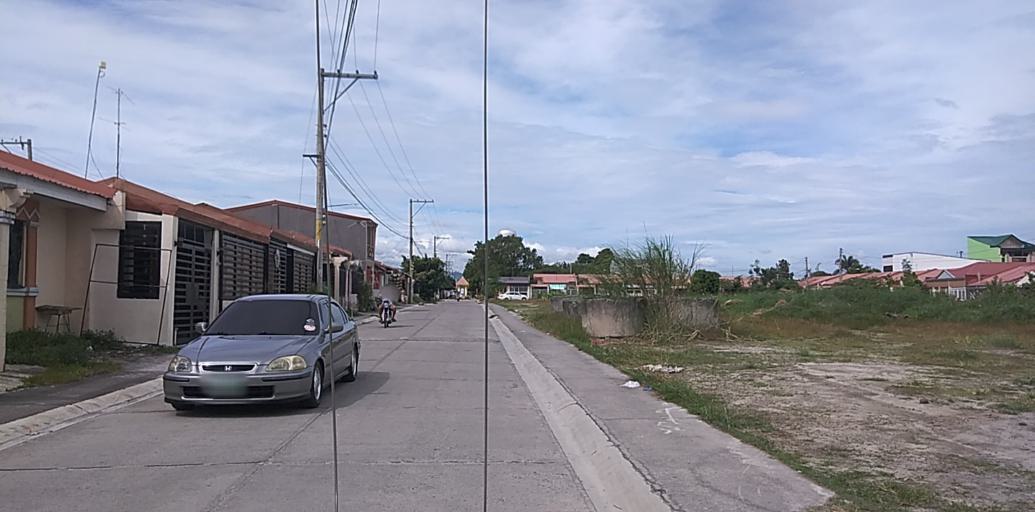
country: PH
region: Central Luzon
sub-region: Province of Pampanga
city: Manibaug Pasig
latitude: 15.1134
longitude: 120.5615
